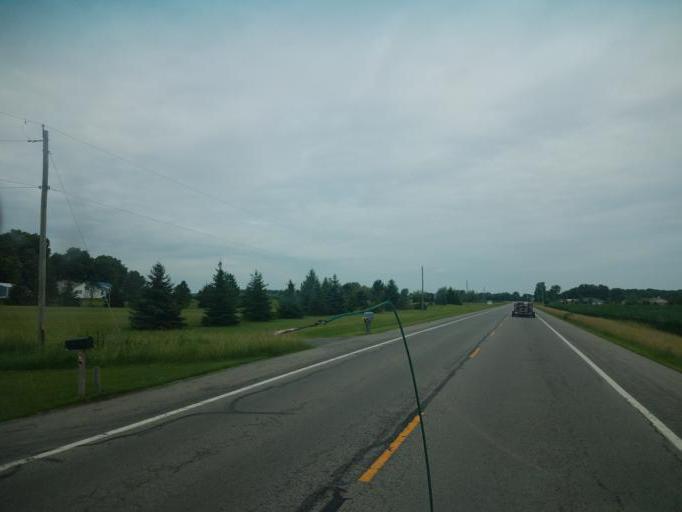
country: US
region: Ohio
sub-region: Hardin County
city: Ada
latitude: 40.7289
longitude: -83.7895
